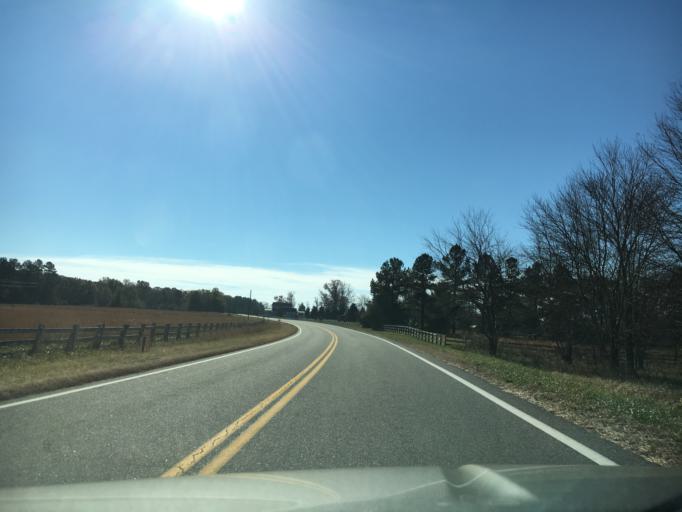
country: US
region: Virginia
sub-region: Cumberland County
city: Cumberland
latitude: 37.5854
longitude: -78.1748
